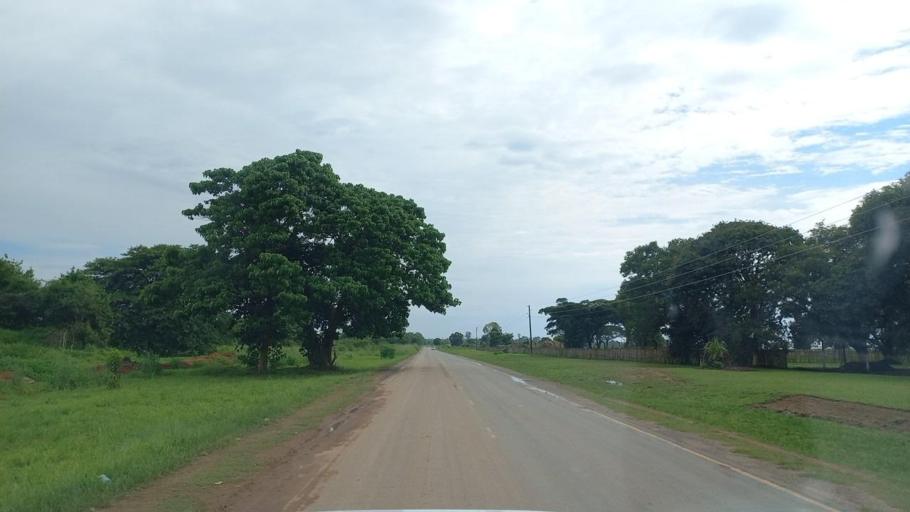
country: ZM
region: Copperbelt
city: Kitwe
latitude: -12.8828
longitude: 28.3184
